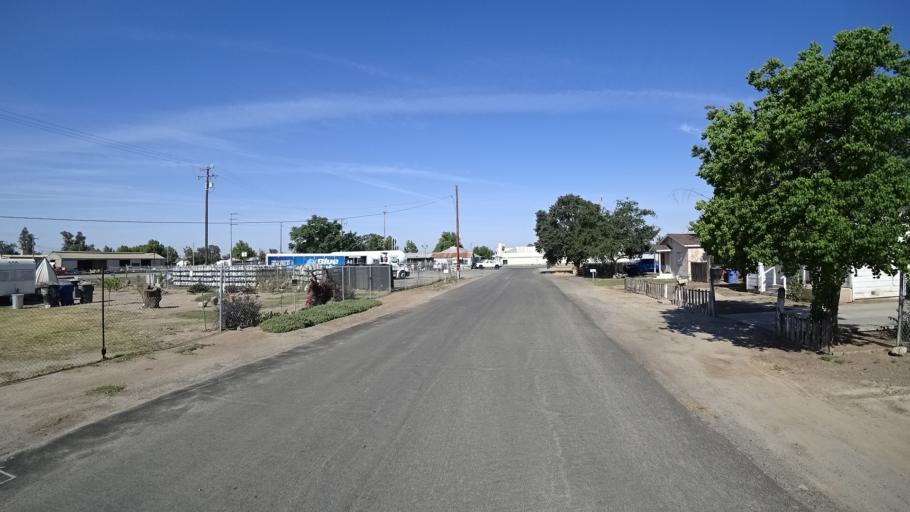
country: US
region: California
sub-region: Kings County
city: Hanford
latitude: 36.3270
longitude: -119.6356
